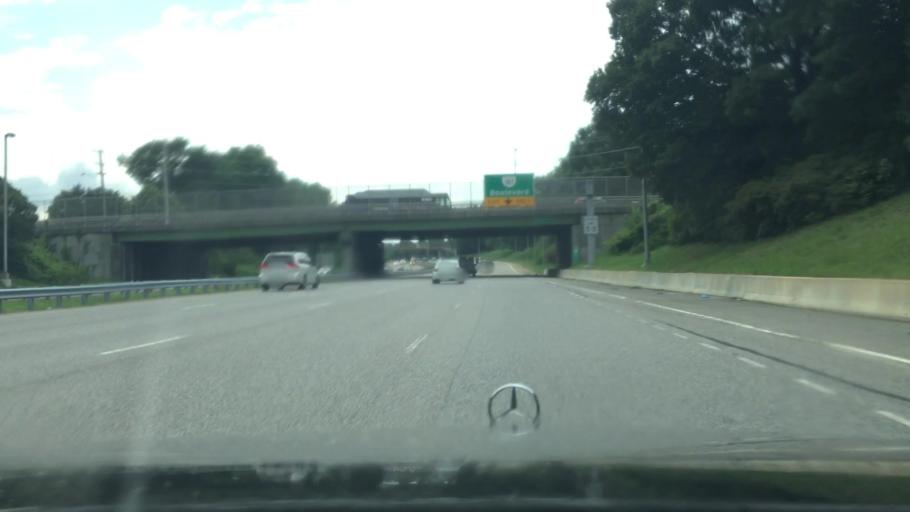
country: US
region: Virginia
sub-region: City of Richmond
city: Richmond
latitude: 37.5467
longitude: -77.4661
